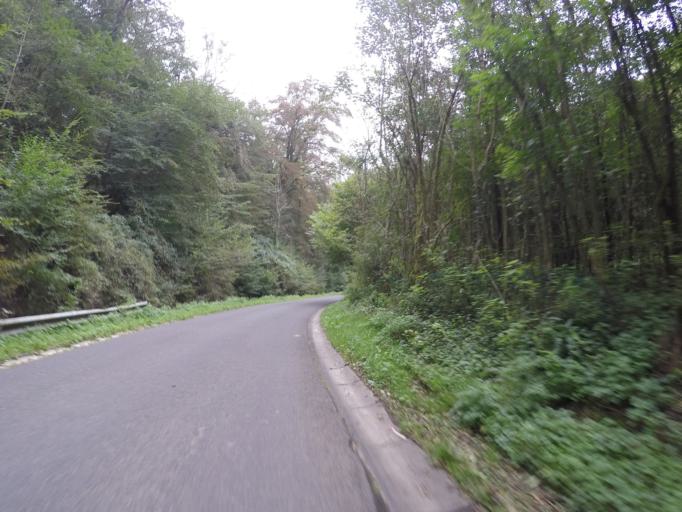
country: BE
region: Wallonia
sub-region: Province de Namur
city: Dinant
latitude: 50.2754
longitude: 4.9443
